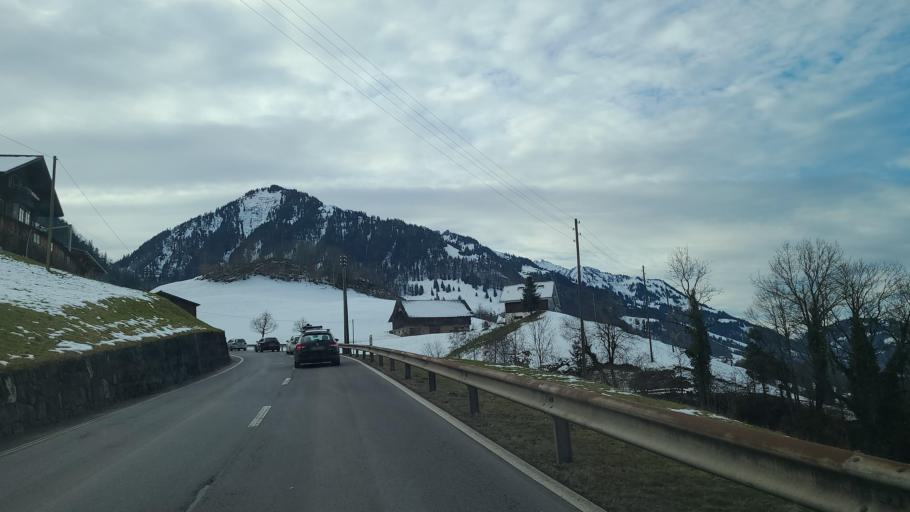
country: CH
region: Obwalden
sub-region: Obwalden
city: Kerns
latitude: 46.8798
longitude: 8.2779
